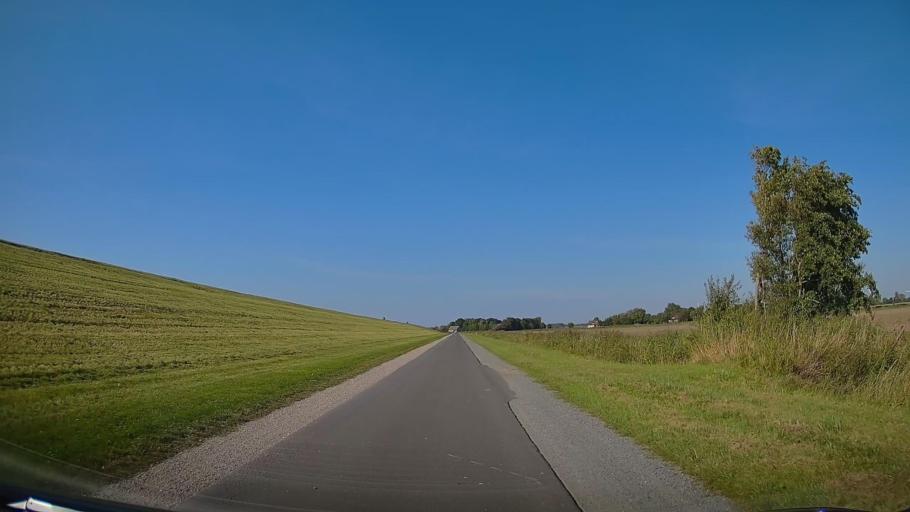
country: DE
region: Lower Saxony
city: Wremen
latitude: 53.6522
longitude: 8.4943
